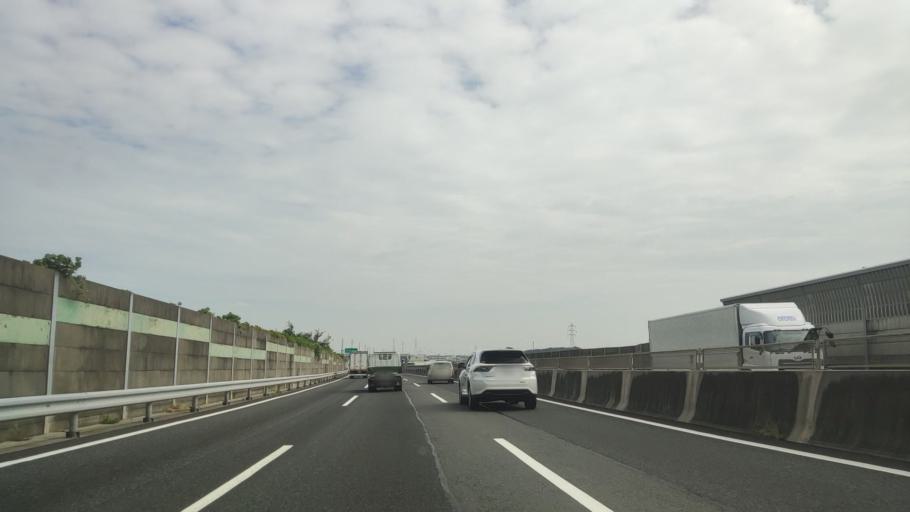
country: JP
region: Mie
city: Komono
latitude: 34.9866
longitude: 136.5428
